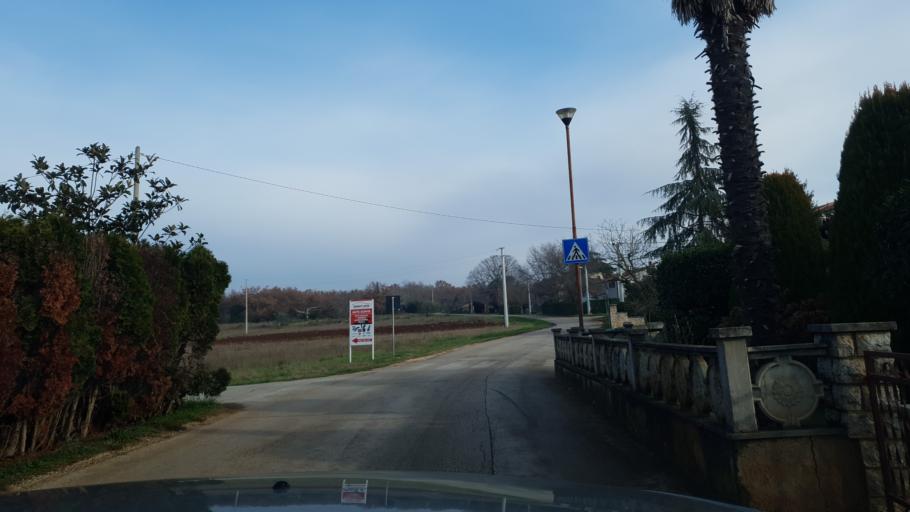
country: HR
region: Istarska
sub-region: Grad Porec
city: Porec
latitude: 45.2394
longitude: 13.6460
